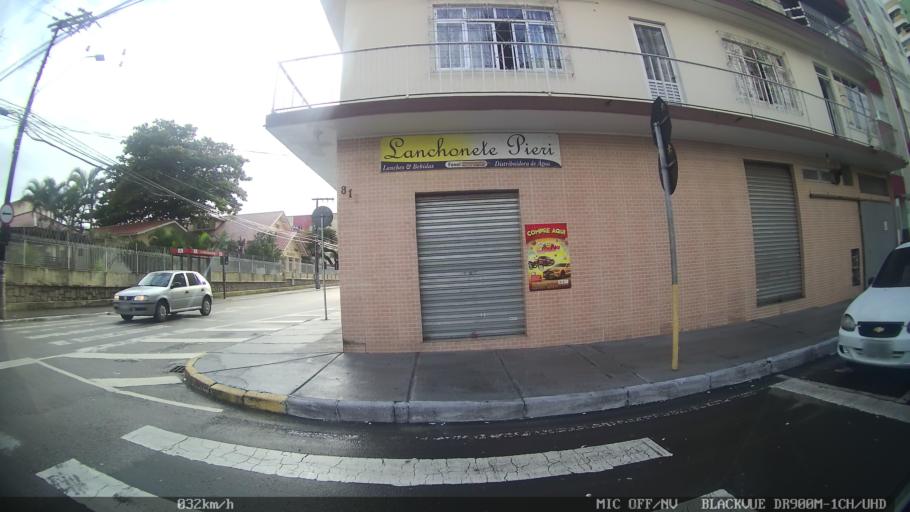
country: BR
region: Santa Catarina
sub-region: Sao Jose
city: Campinas
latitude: -27.5937
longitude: -48.6112
